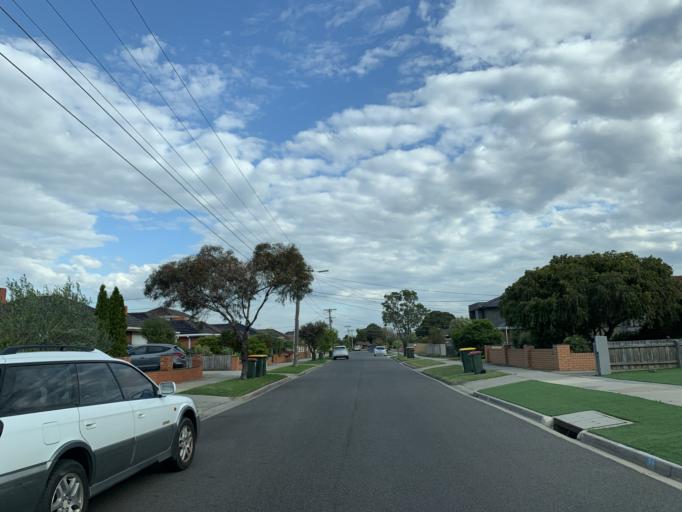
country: AU
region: Victoria
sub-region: Moonee Valley
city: Essendon West
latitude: -37.7561
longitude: 144.8583
